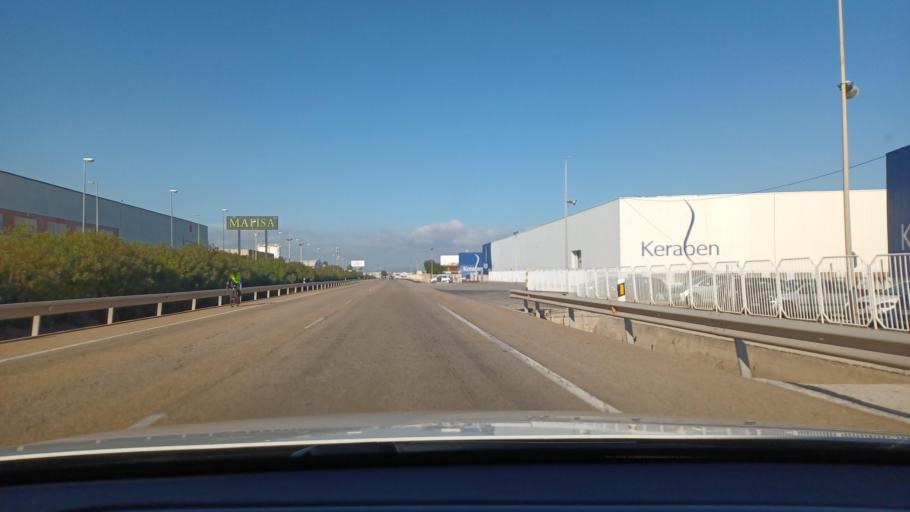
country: ES
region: Valencia
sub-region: Provincia de Castello
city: Moncofar
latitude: 39.8250
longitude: -0.1654
